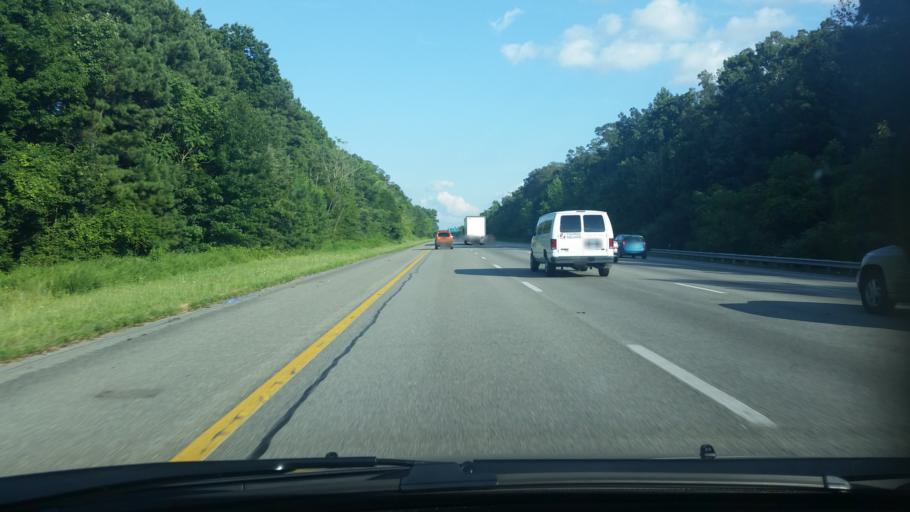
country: US
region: Virginia
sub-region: Hanover County
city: Mechanicsville
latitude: 37.5912
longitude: -77.3441
